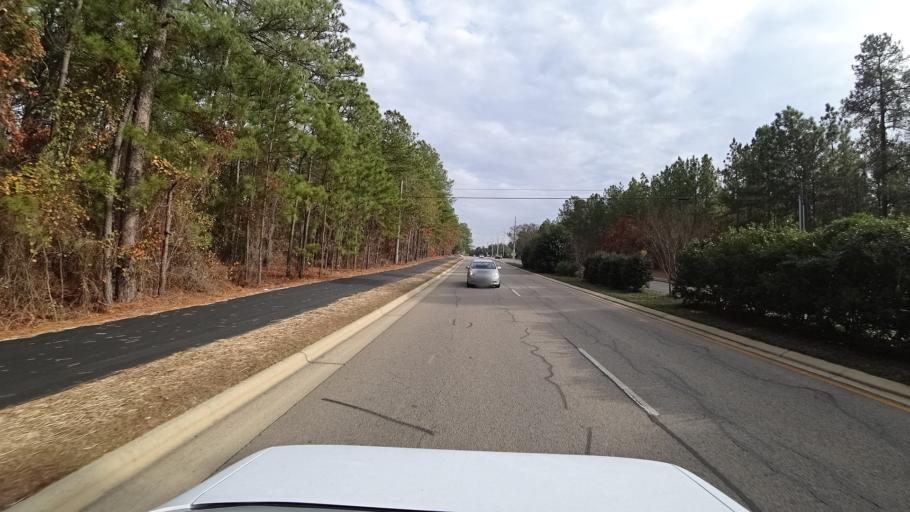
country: US
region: North Carolina
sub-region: Moore County
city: Southern Pines
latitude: 35.1742
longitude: -79.4138
